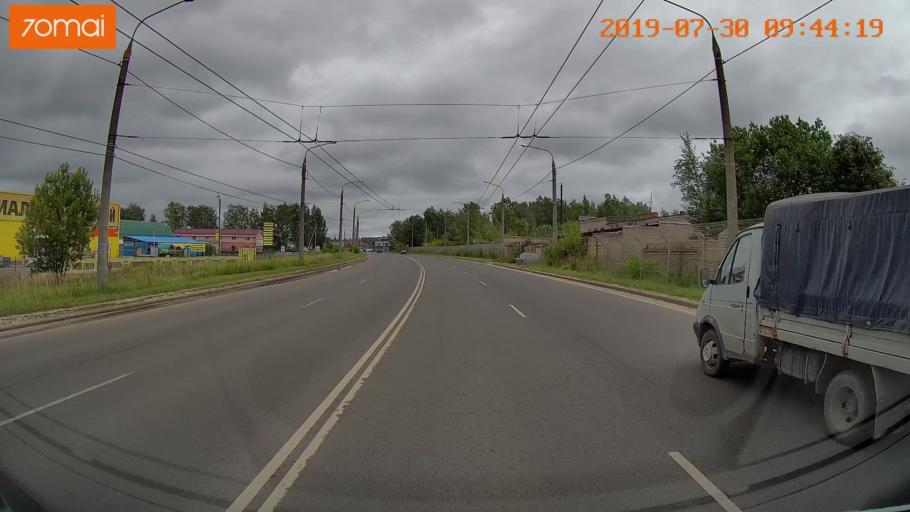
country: RU
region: Ivanovo
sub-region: Gorod Ivanovo
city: Ivanovo
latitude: 56.9484
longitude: 40.9620
